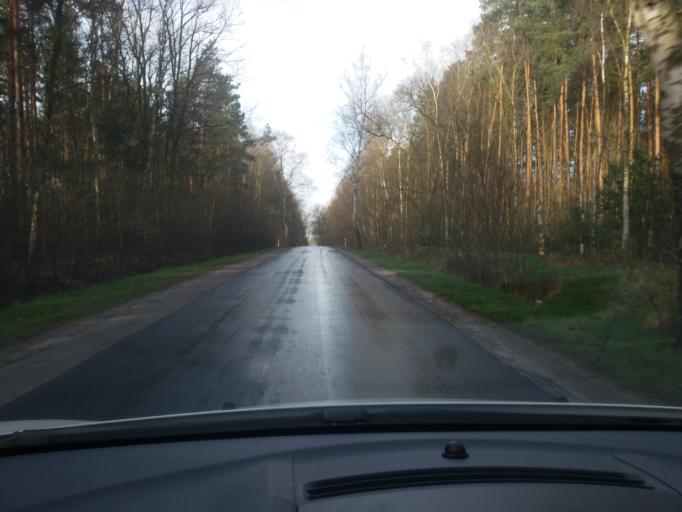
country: PL
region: Lubusz
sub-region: Powiat nowosolski
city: Bytom Odrzanski
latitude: 51.7188
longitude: 15.7765
